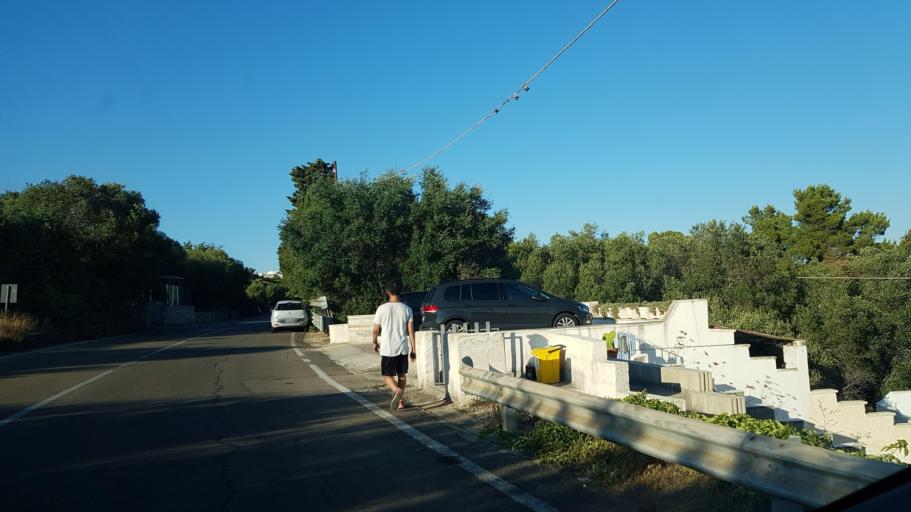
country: IT
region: Apulia
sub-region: Provincia di Lecce
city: Castro
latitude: 39.9984
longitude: 18.4185
